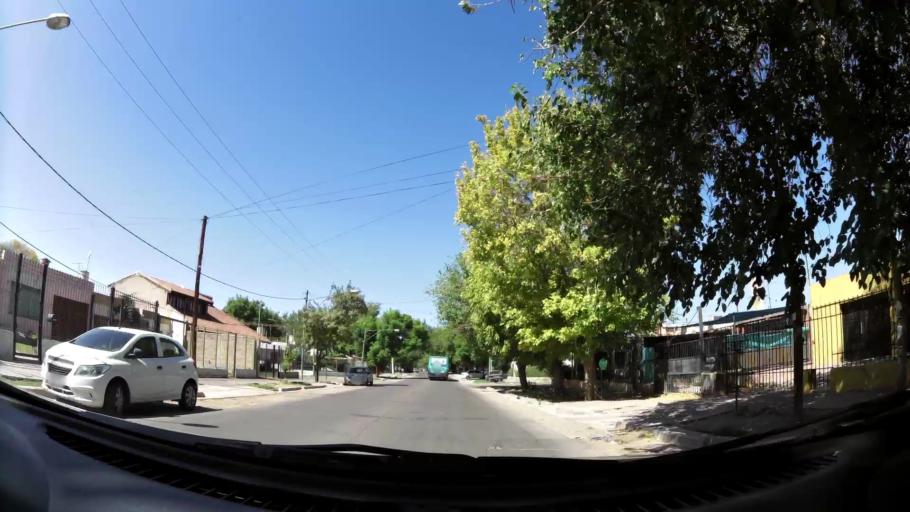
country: AR
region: Mendoza
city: Mendoza
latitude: -32.8856
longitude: -68.8081
